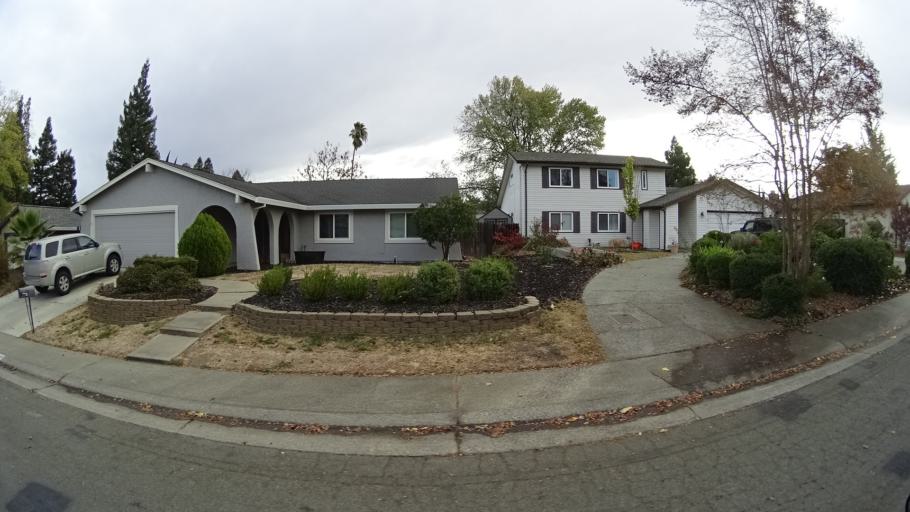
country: US
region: California
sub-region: Sacramento County
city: Citrus Heights
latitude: 38.7180
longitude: -121.2489
